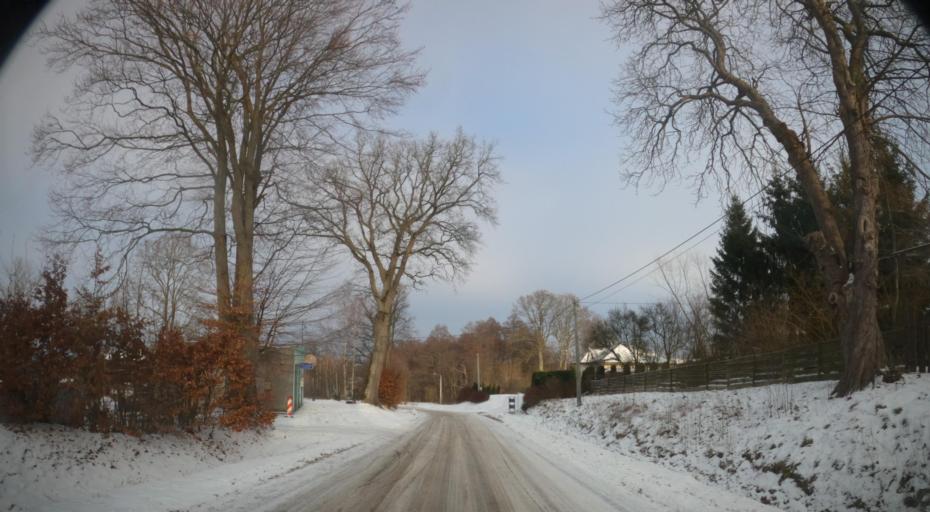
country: PL
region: West Pomeranian Voivodeship
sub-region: Powiat slawienski
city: Darlowo
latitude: 54.2918
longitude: 16.4327
